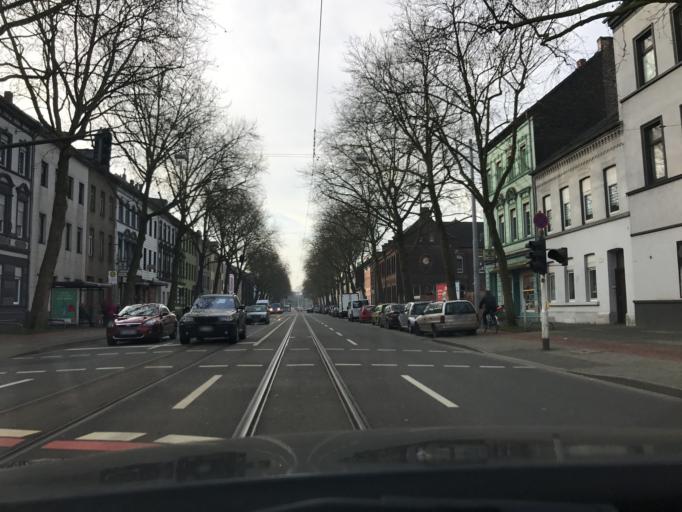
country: DE
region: North Rhine-Westphalia
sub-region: Regierungsbezirk Dusseldorf
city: Krefeld
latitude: 51.3164
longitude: 6.5595
